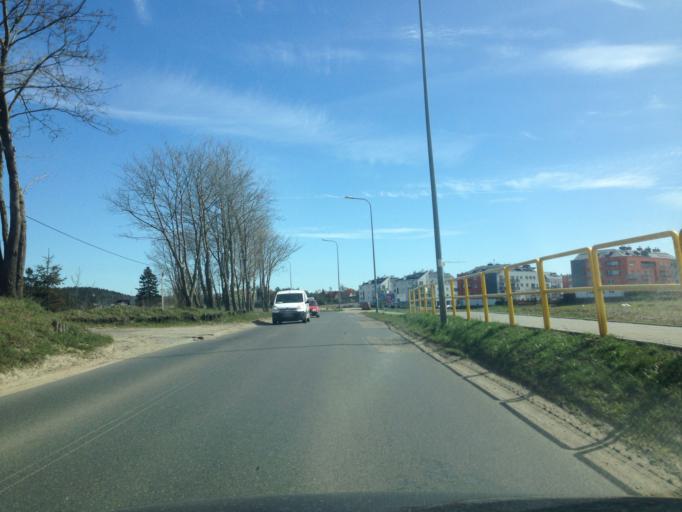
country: PL
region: Pomeranian Voivodeship
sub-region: Powiat wejherowski
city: Bojano
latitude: 54.4891
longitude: 18.4260
